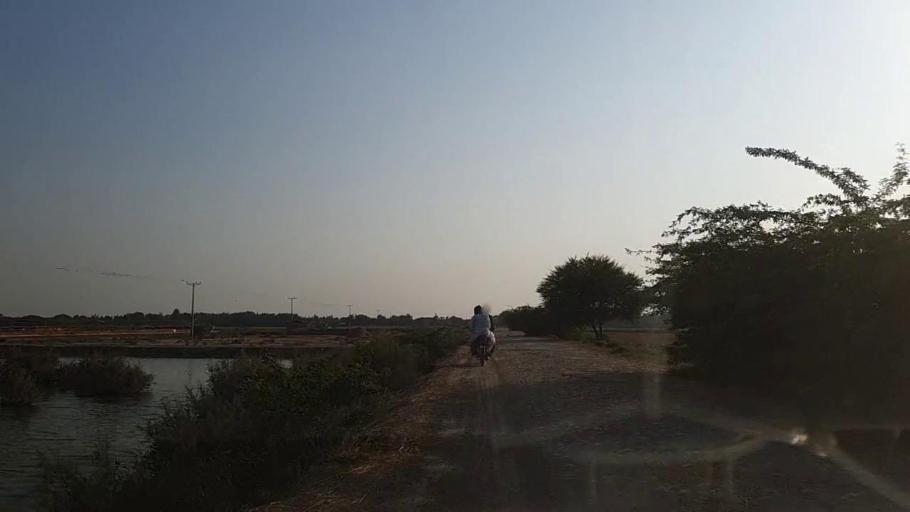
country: PK
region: Sindh
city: Mirpur Batoro
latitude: 24.7590
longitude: 68.2315
